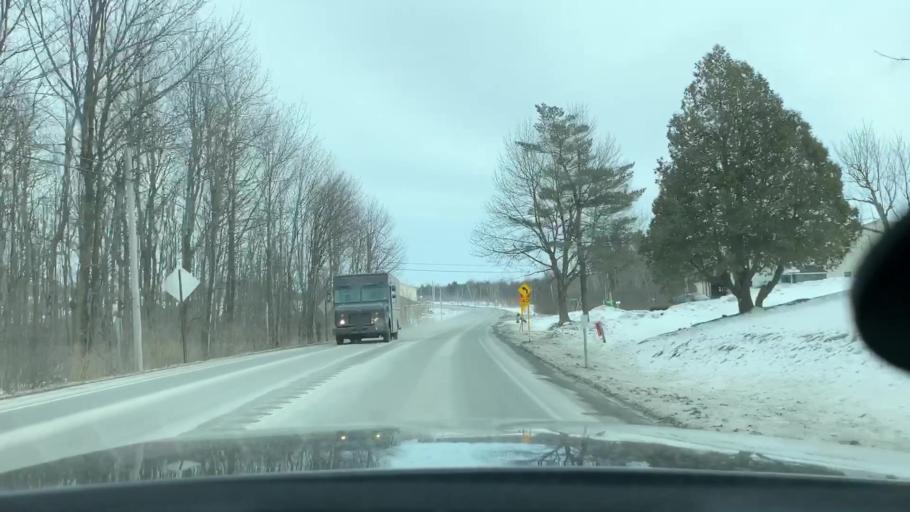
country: US
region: New York
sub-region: Oneida County
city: Utica
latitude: 43.0350
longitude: -75.1871
